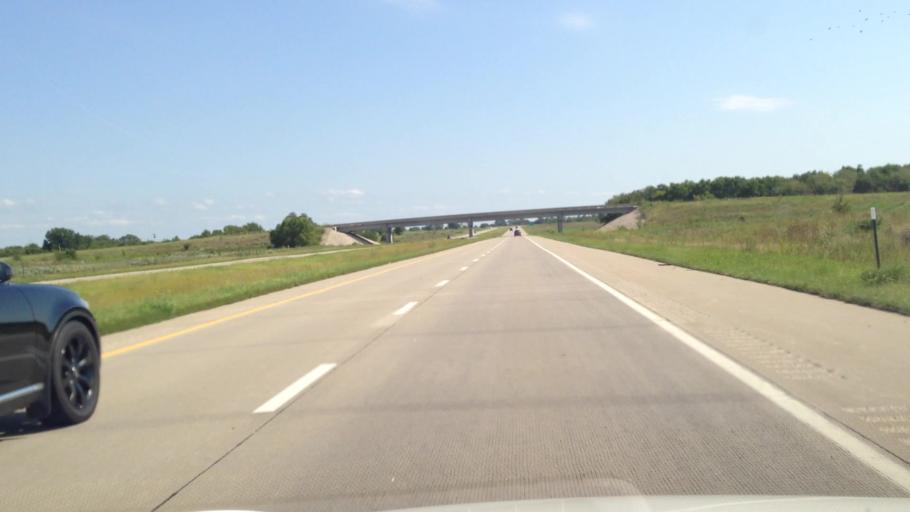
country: US
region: Kansas
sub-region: Linn County
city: La Cygne
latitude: 38.2895
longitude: -94.6751
